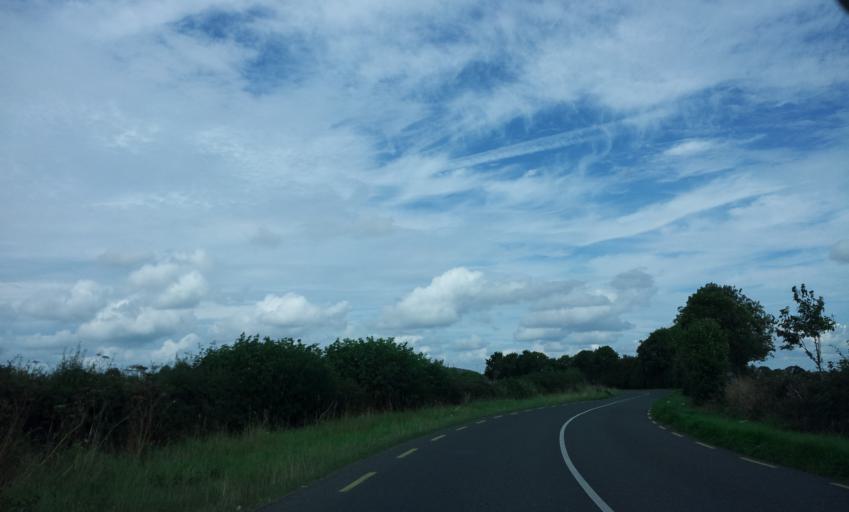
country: IE
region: Leinster
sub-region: Laois
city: Stradbally
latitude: 52.9733
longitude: -7.2132
